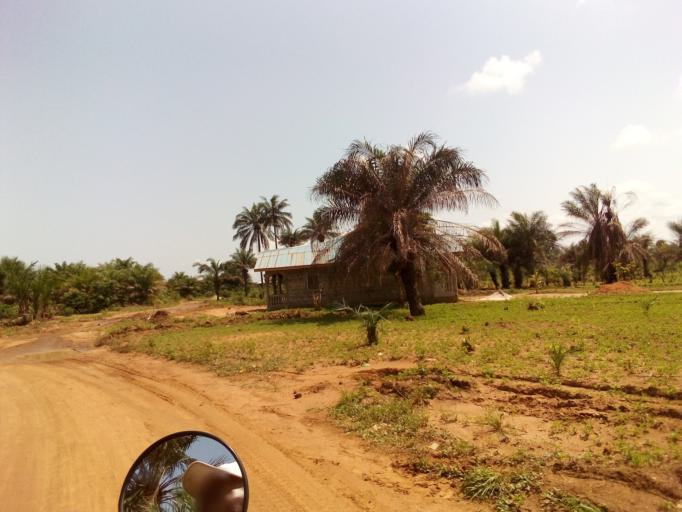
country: SL
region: Western Area
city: Waterloo
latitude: 8.3432
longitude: -13.0121
